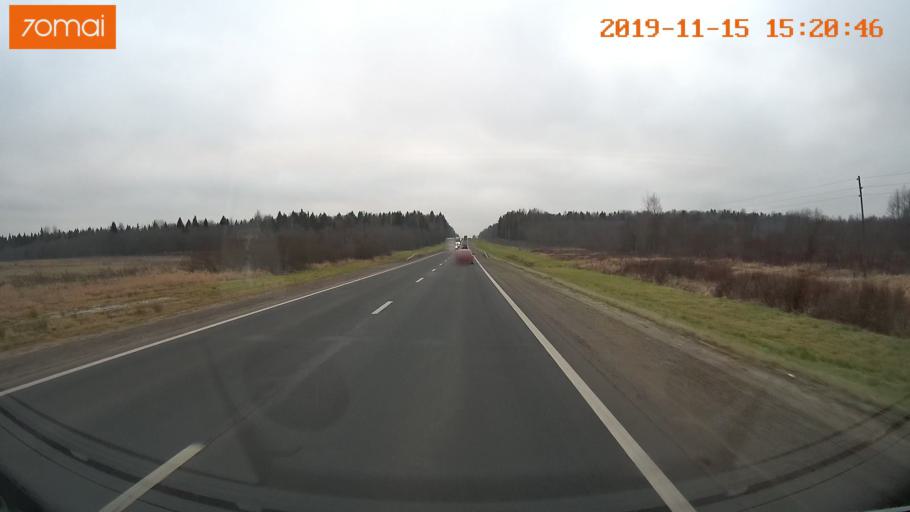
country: RU
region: Jaroslavl
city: Danilov
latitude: 58.2201
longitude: 40.1566
